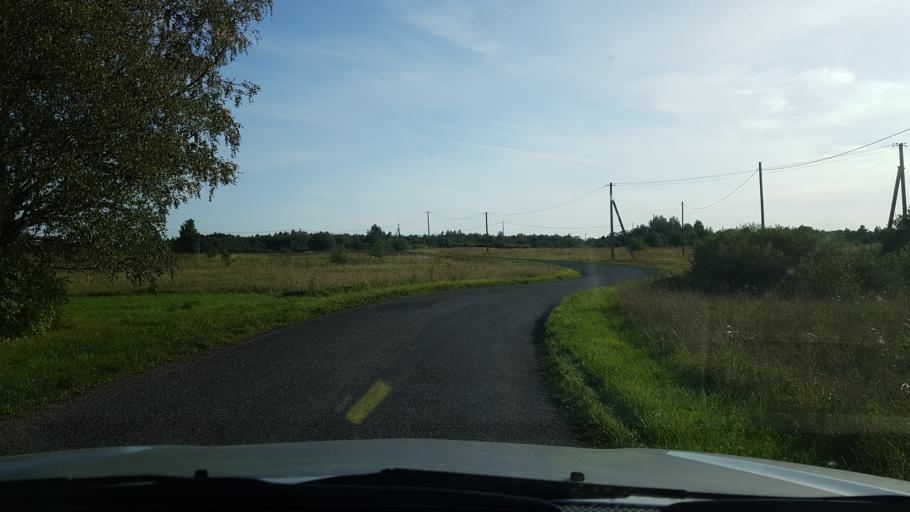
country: EE
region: Ida-Virumaa
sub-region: Narva-Joesuu linn
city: Narva-Joesuu
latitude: 59.3500
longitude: 28.0289
